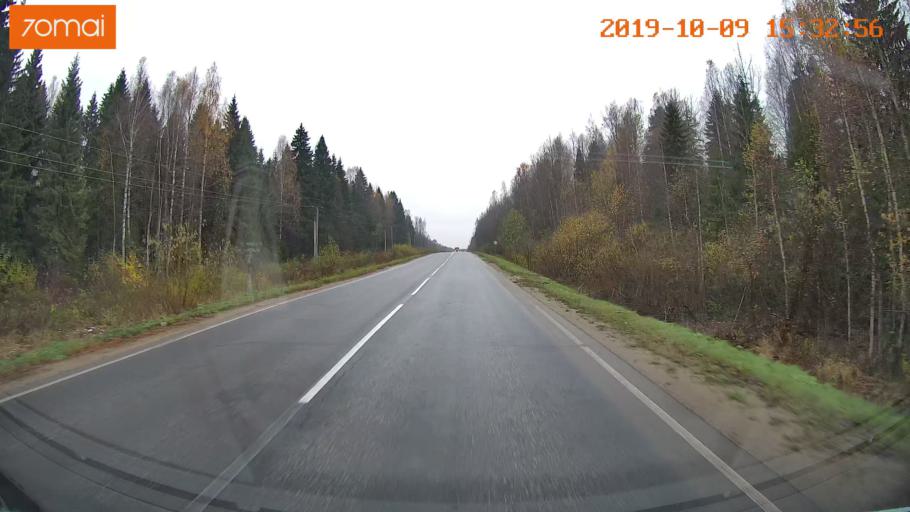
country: RU
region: Kostroma
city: Oktyabr'skiy
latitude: 57.9585
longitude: 41.2692
